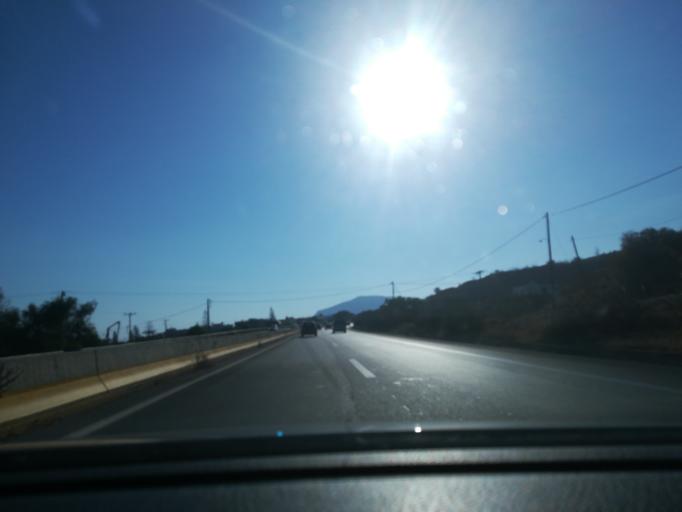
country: GR
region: Crete
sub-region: Nomos Irakleiou
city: Gournes
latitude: 35.3285
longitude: 25.2691
